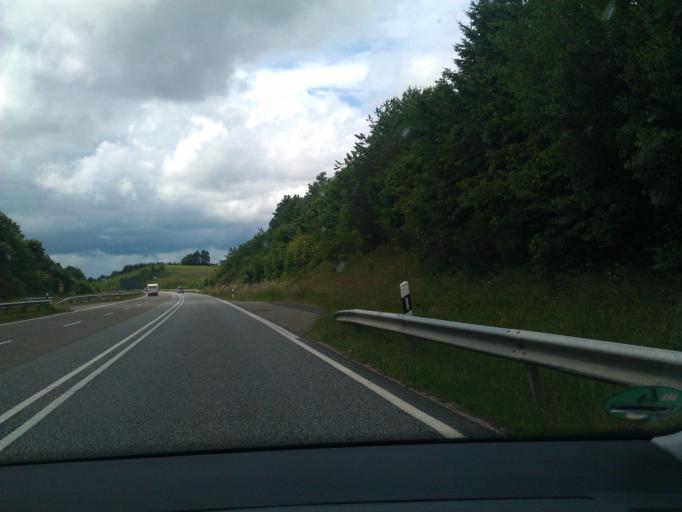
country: DE
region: Rheinland-Pfalz
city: Grosslangenfeld
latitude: 50.2150
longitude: 6.2372
